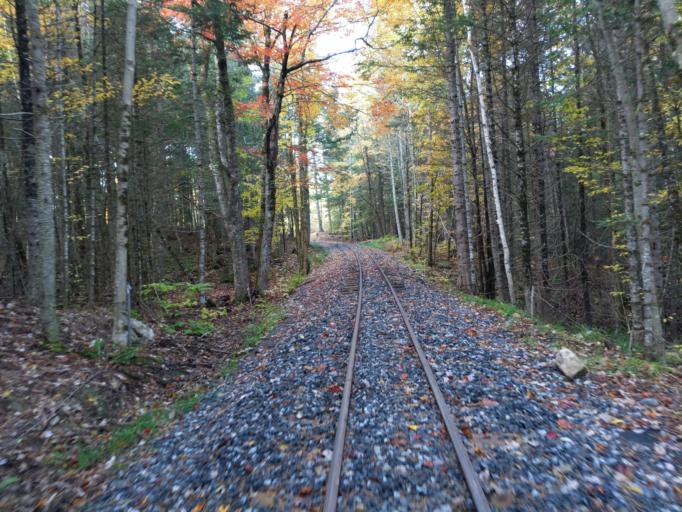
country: US
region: Maine
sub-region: Lincoln County
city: Whitefield
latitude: 44.0986
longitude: -69.6226
